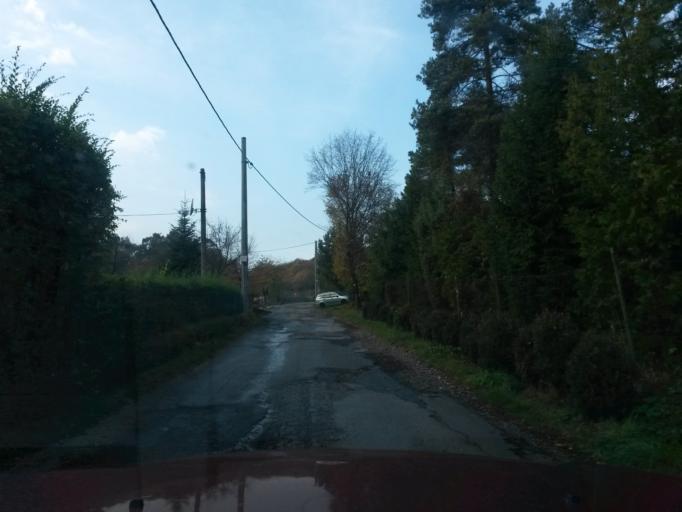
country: SK
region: Kosicky
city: Kosice
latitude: 48.7512
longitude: 21.2277
